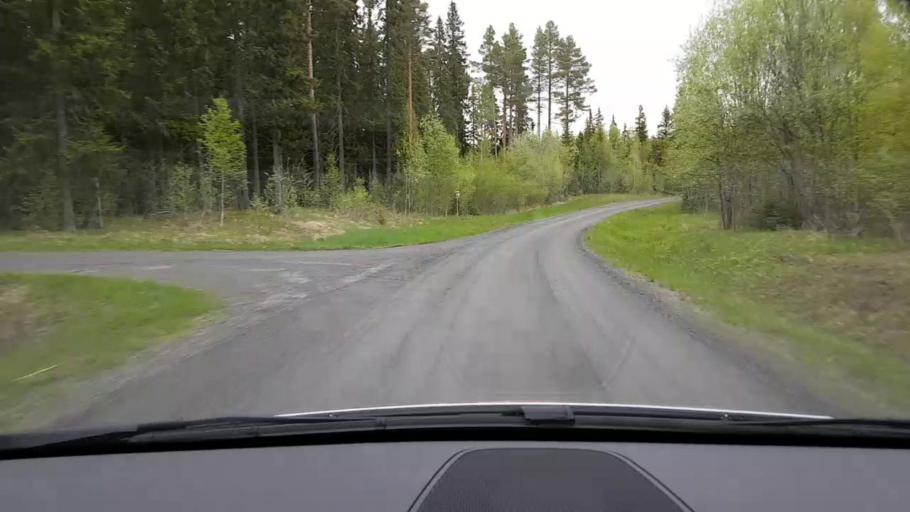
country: SE
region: Jaemtland
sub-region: Krokoms Kommun
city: Krokom
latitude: 63.2967
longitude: 14.3931
